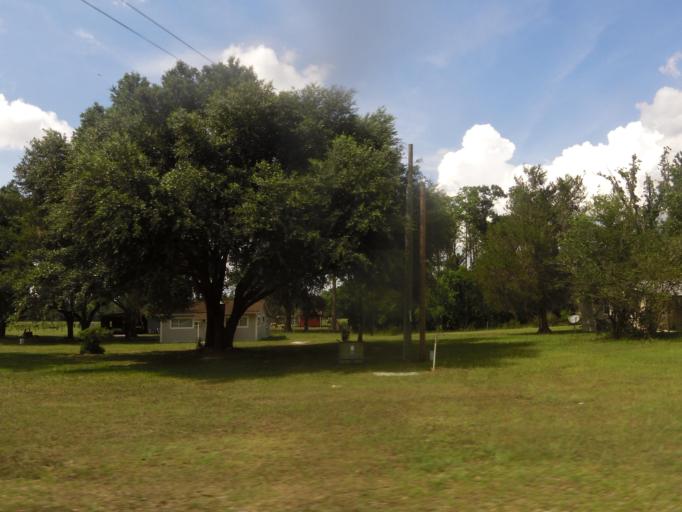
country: US
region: Florida
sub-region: Baker County
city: Macclenny
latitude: 30.2012
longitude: -82.0452
